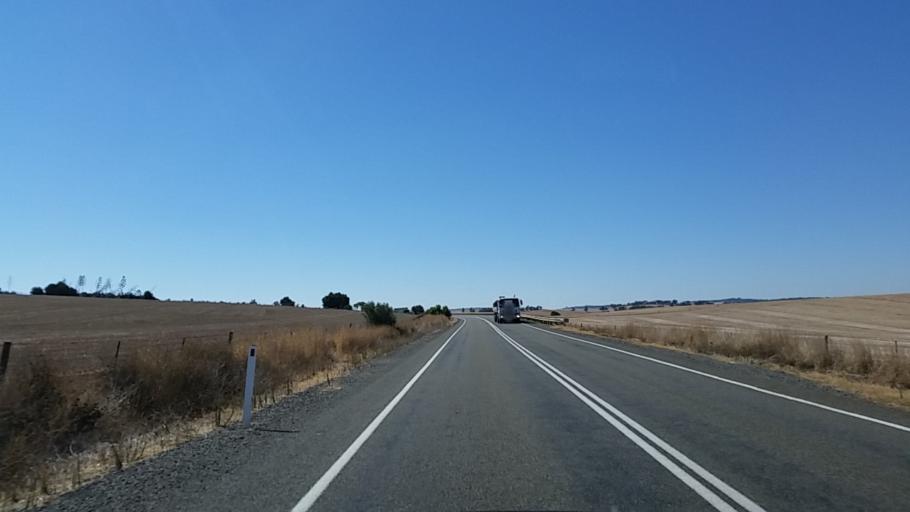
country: AU
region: South Australia
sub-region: Clare and Gilbert Valleys
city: Clare
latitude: -34.0688
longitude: 138.7896
